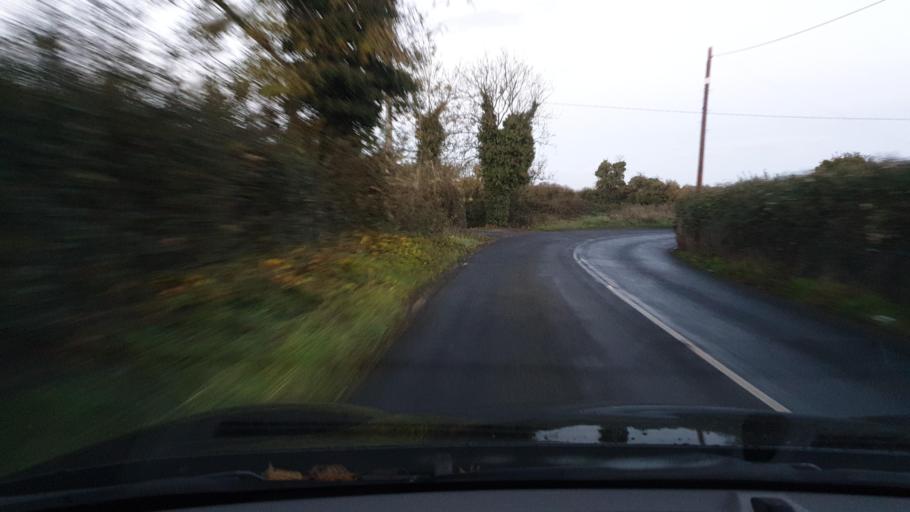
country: IE
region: Leinster
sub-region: An Mhi
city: Ashbourne
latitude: 53.5103
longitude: -6.4288
